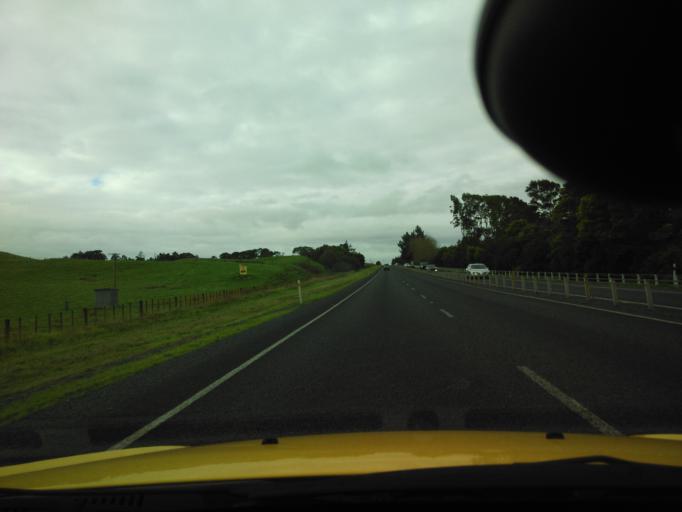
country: NZ
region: Waikato
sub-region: Waikato District
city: Te Kauwhata
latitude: -37.3760
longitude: 175.0970
